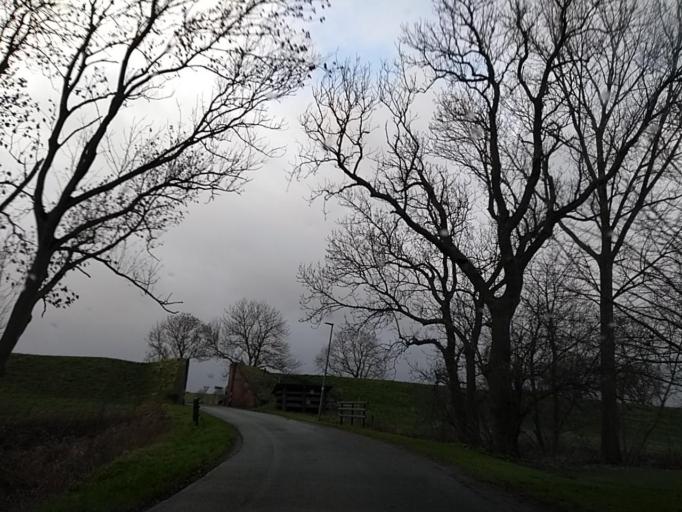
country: DE
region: Lower Saxony
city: Bunde
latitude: 53.2623
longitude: 7.2429
